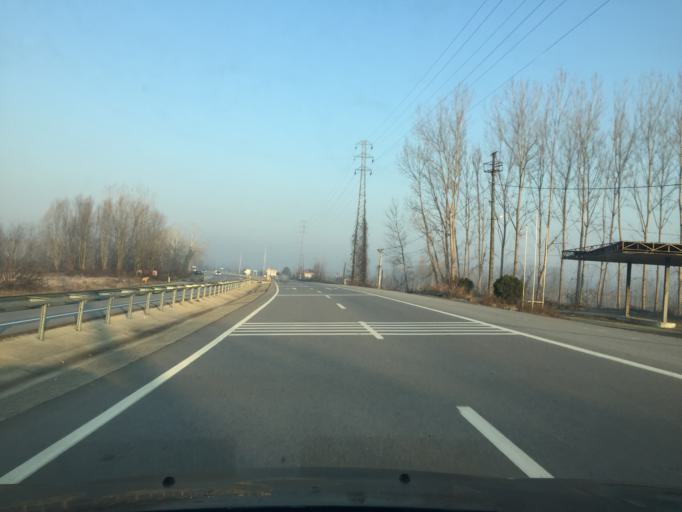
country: TR
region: Sakarya
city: Akyazi
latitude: 40.6944
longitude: 30.5722
